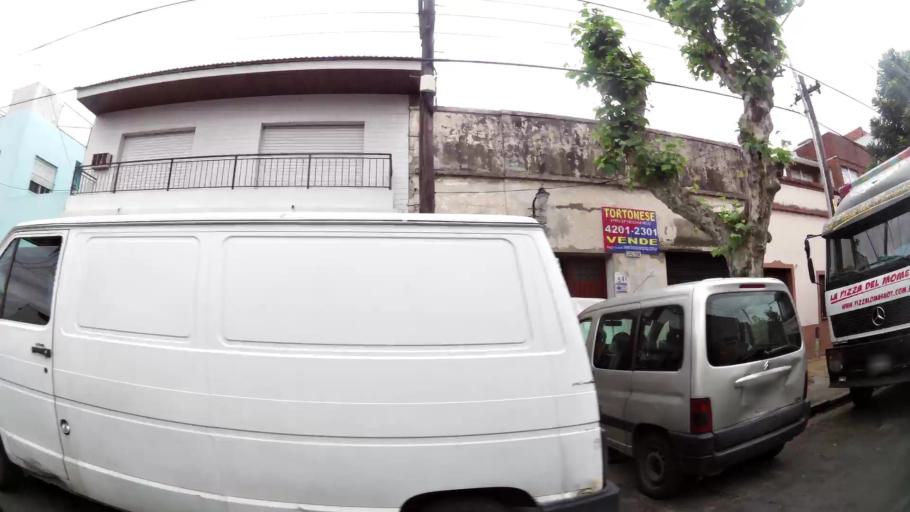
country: AR
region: Buenos Aires
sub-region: Partido de Avellaneda
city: Avellaneda
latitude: -34.6748
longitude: -58.3895
